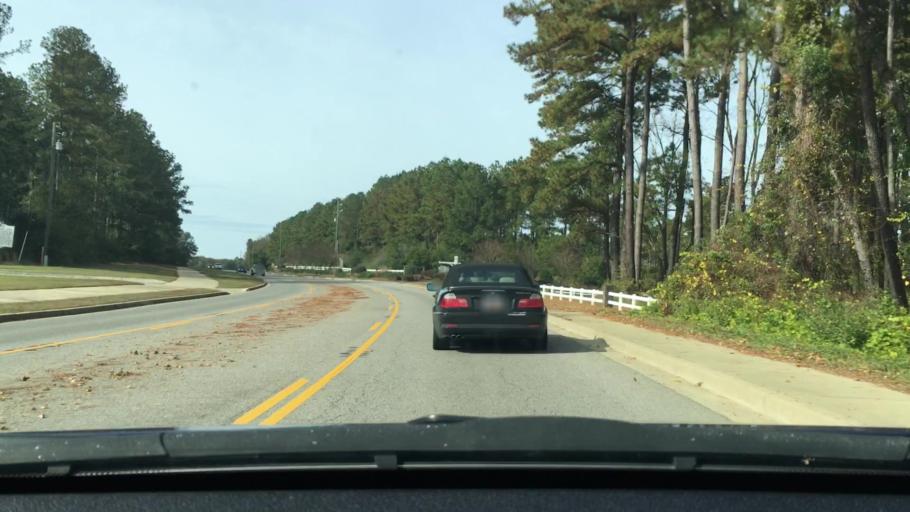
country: US
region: South Carolina
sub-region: Sumter County
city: South Sumter
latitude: 33.9191
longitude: -80.3928
